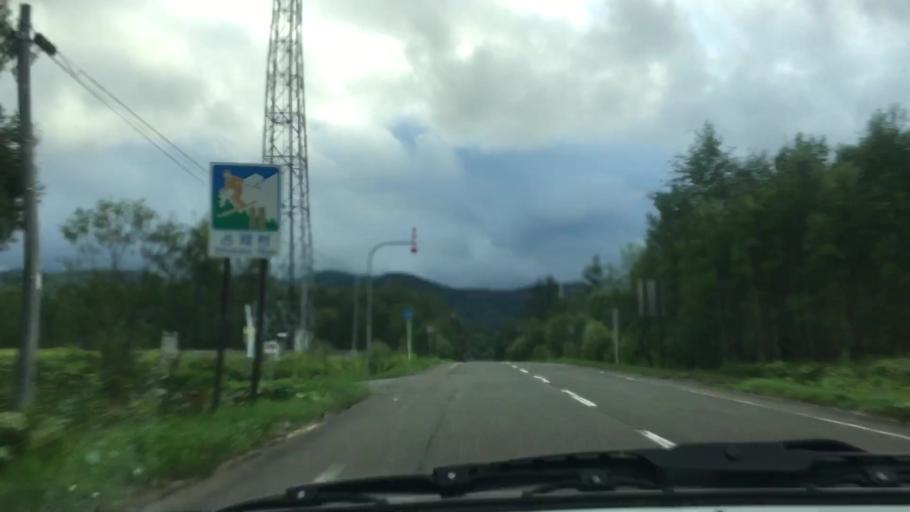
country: JP
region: Hokkaido
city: Shimo-furano
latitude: 43.0487
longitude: 142.6664
